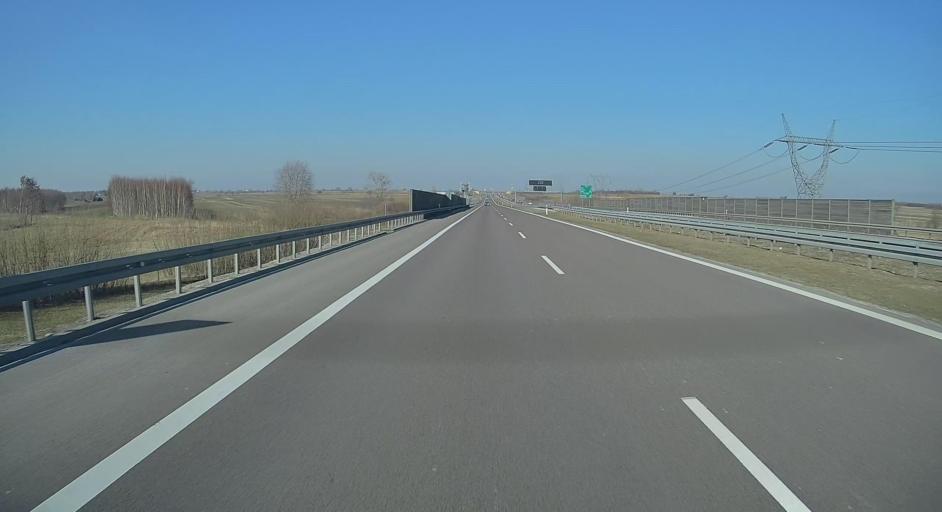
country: PL
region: Lublin Voivodeship
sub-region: Powiat pulawski
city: Markuszow
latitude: 51.3827
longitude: 22.2782
